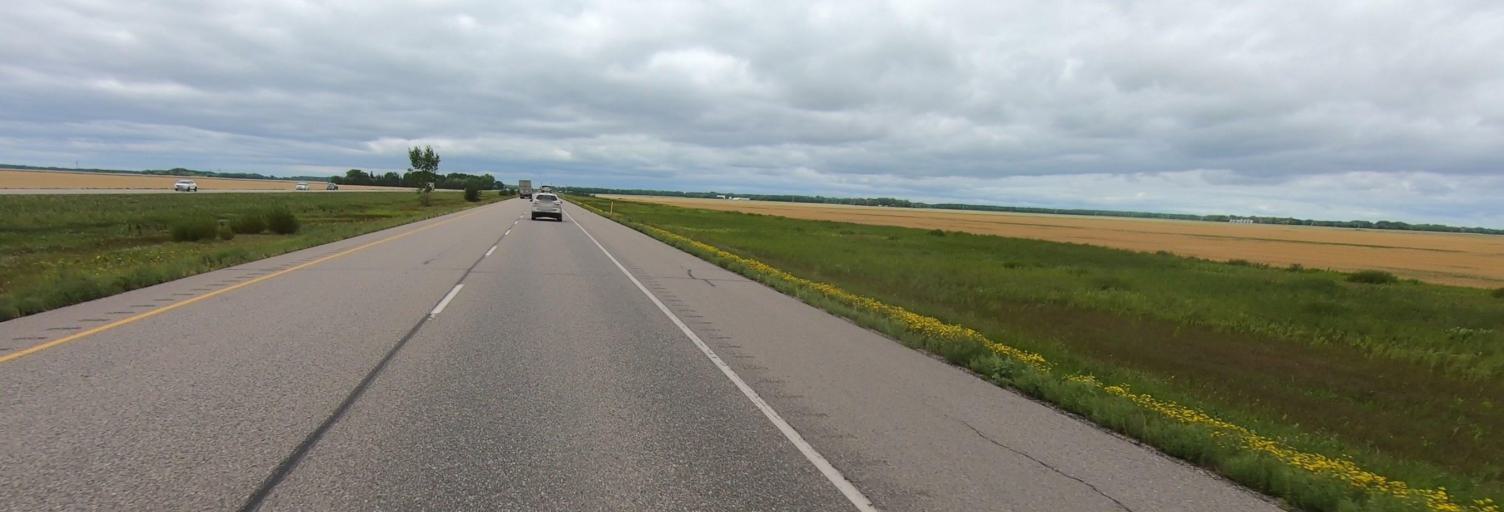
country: CA
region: Manitoba
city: Portage la Prairie
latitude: 49.9588
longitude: -98.0343
